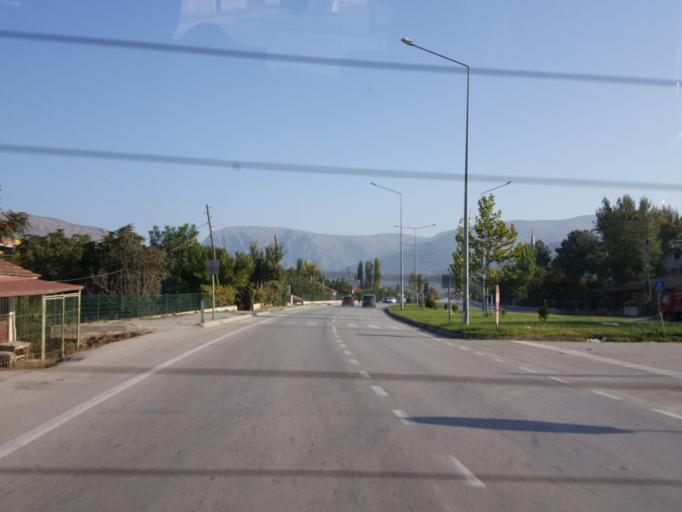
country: TR
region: Amasya
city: Amasya
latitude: 40.5942
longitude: 35.8029
